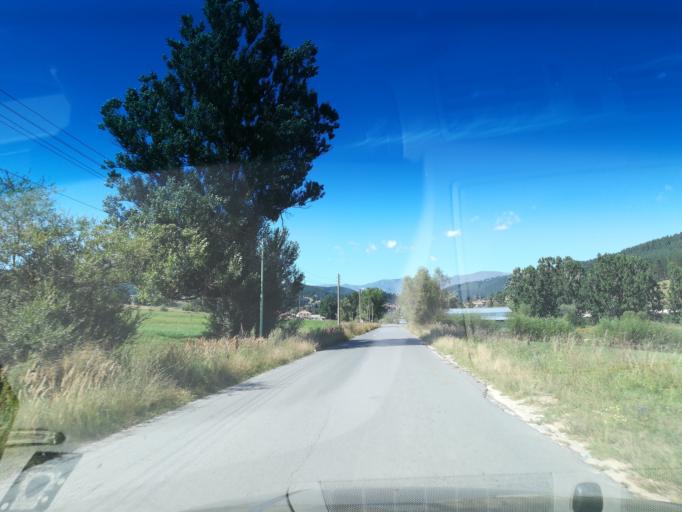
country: BG
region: Sofiya
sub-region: Obshtina Koprivshtitsa
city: Koprivshtitsa
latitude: 42.6239
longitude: 24.3672
